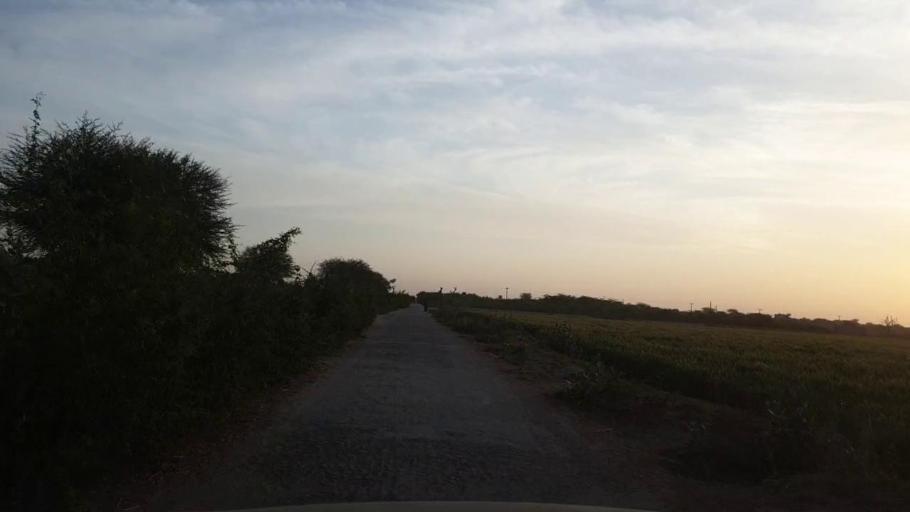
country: PK
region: Sindh
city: Kunri
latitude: 25.1198
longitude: 69.5670
